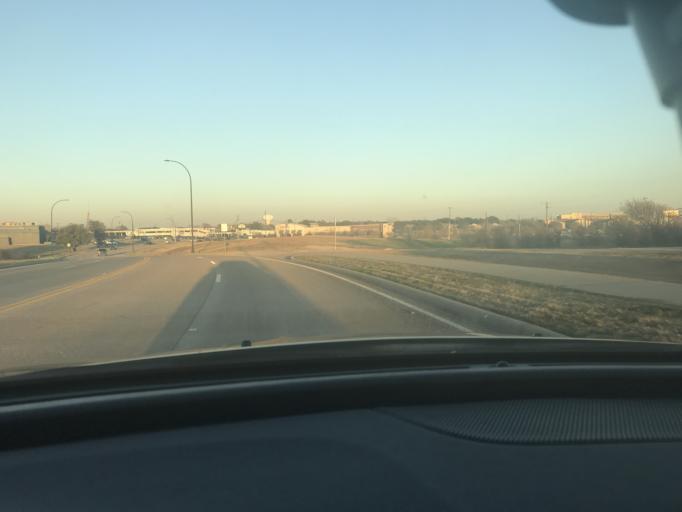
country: US
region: Texas
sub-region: Tarrant County
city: Arlington
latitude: 32.7618
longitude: -97.1003
